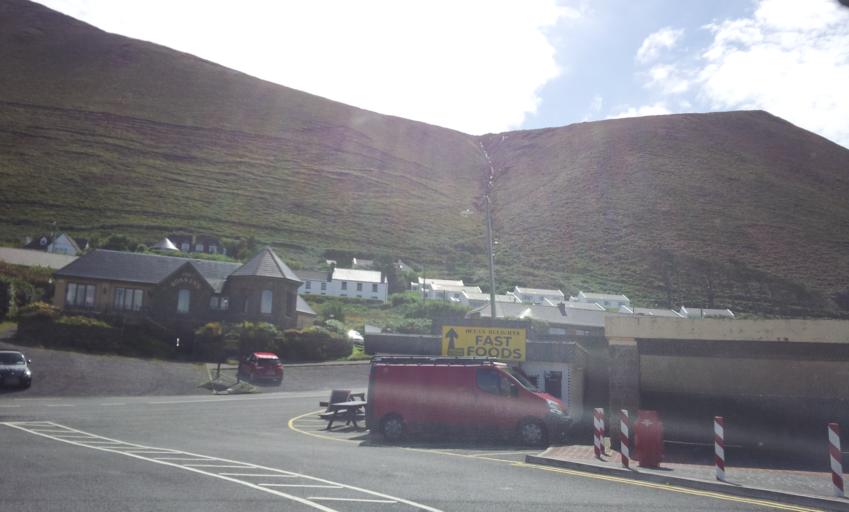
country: IE
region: Munster
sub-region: Ciarrai
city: Killorglin
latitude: 52.0543
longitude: -9.9763
